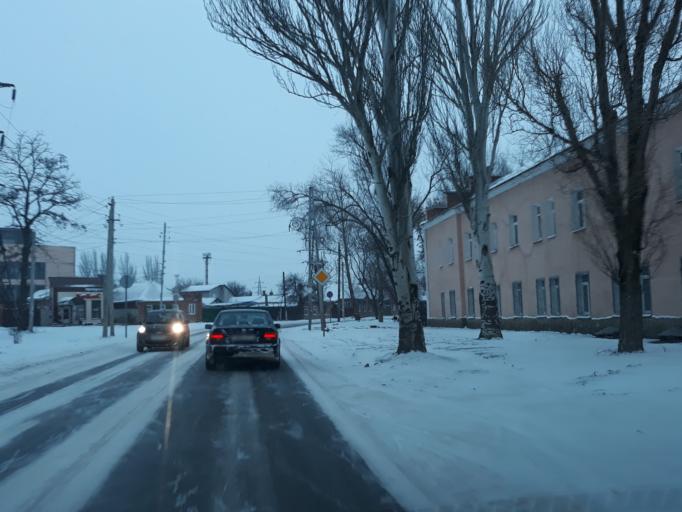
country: RU
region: Rostov
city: Taganrog
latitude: 47.2527
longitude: 38.9348
